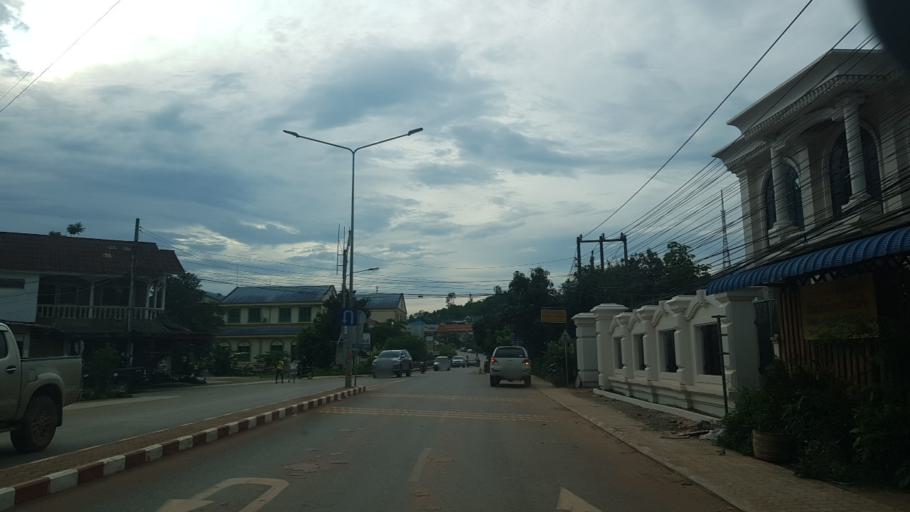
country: LA
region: Oudomxai
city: Muang Xay
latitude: 20.6893
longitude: 101.9847
